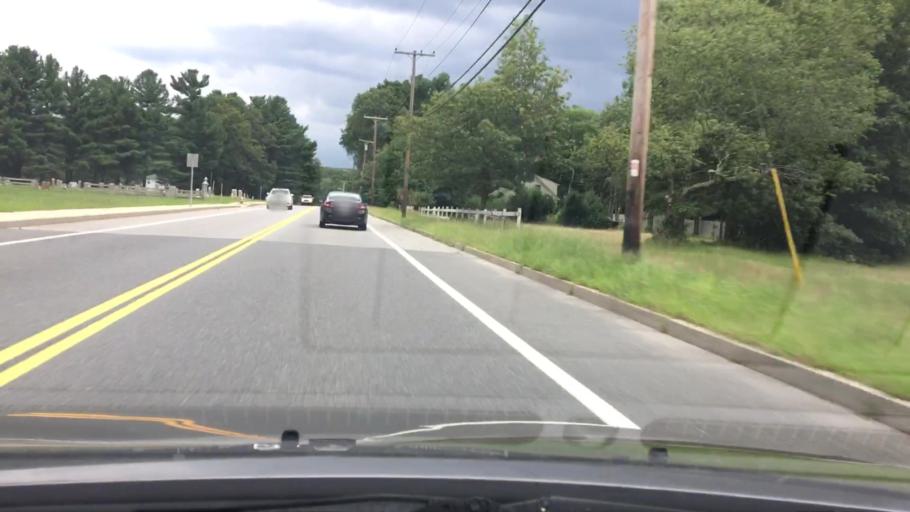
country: US
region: Rhode Island
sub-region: Providence County
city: Cumberland
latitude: 41.9806
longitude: -71.3994
